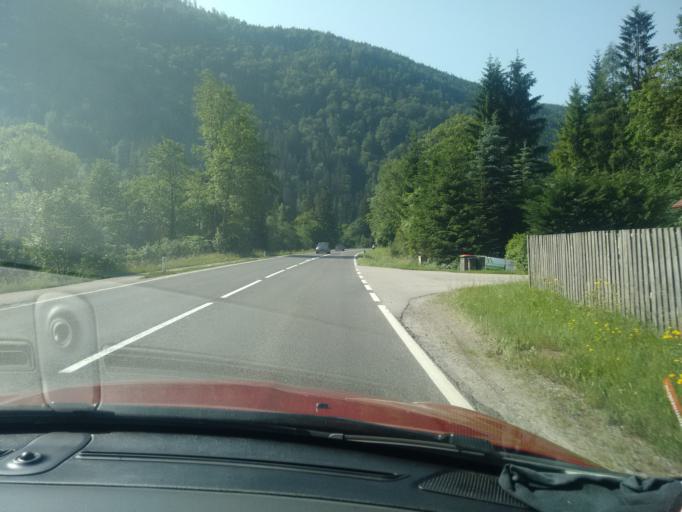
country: AT
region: Upper Austria
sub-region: Politischer Bezirk Gmunden
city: Bad Ischl
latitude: 47.7323
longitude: 13.6590
